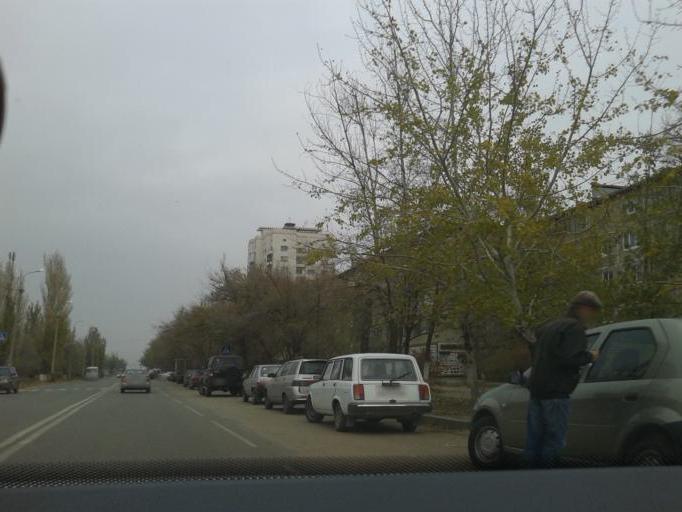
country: RU
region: Volgograd
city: Gorodishche
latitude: 48.7633
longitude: 44.4785
